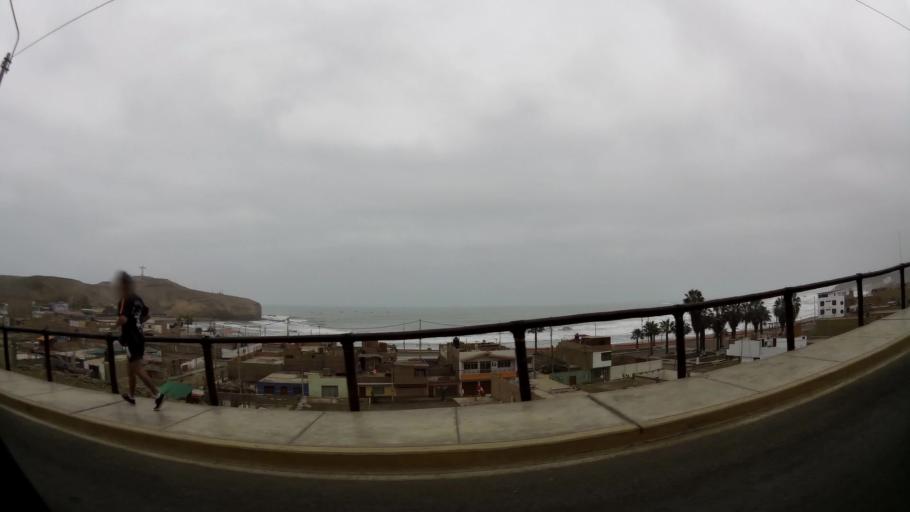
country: PE
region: Lima
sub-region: Barranca
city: Barranca
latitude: -10.7656
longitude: -77.7601
